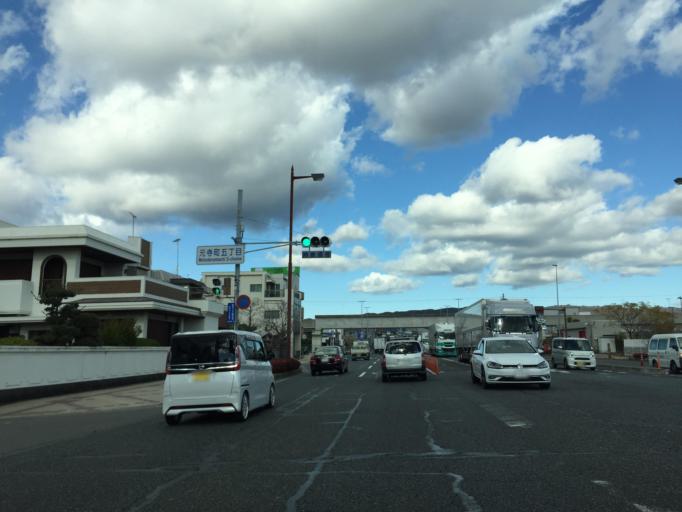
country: JP
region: Wakayama
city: Wakayama-shi
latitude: 34.2403
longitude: 135.1768
